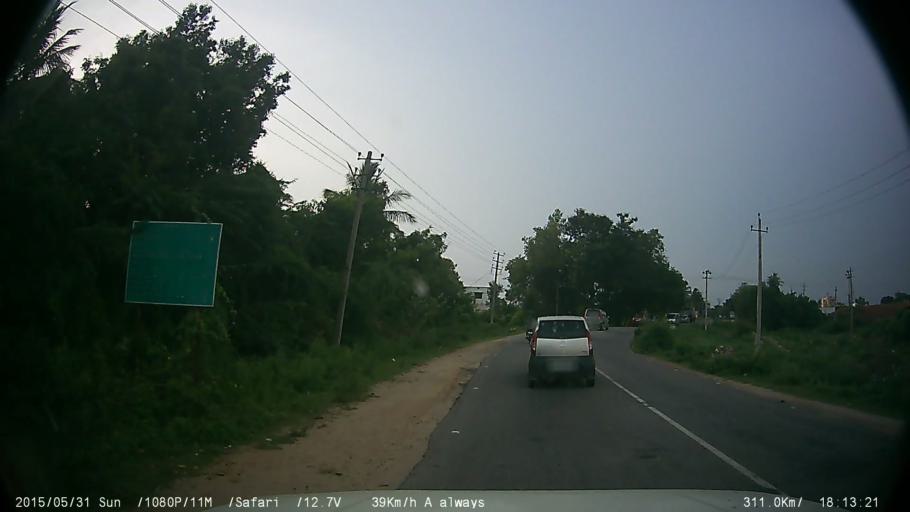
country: IN
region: Karnataka
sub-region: Mysore
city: Nanjangud
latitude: 12.1021
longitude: 76.6714
